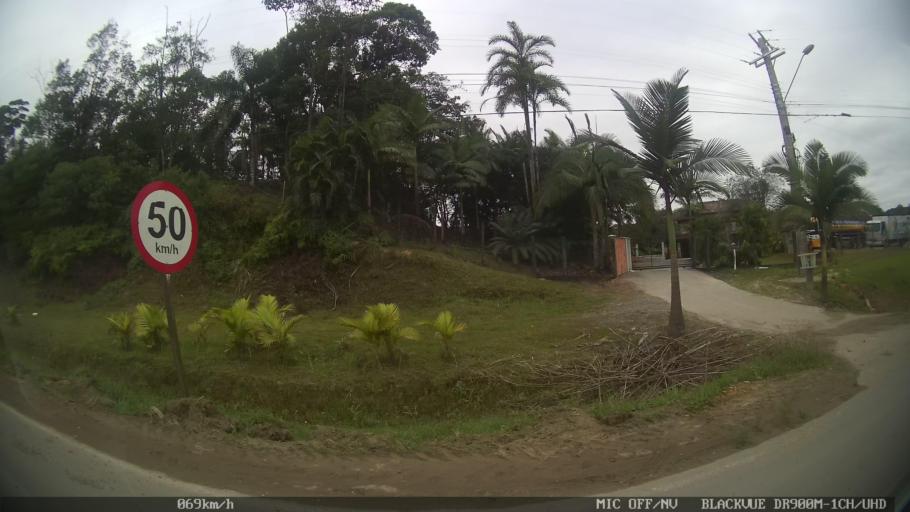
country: BR
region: Santa Catarina
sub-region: Joinville
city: Joinville
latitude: -26.2657
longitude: -48.9197
